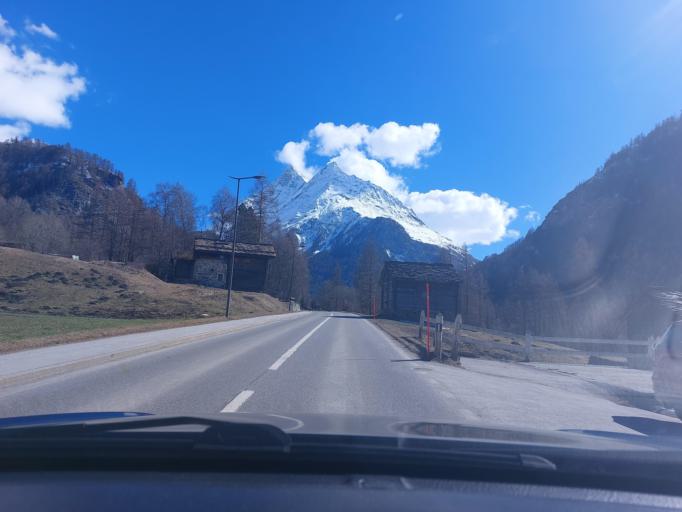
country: CH
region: Valais
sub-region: Herens District
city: Evolene
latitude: 46.1045
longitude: 7.5026
